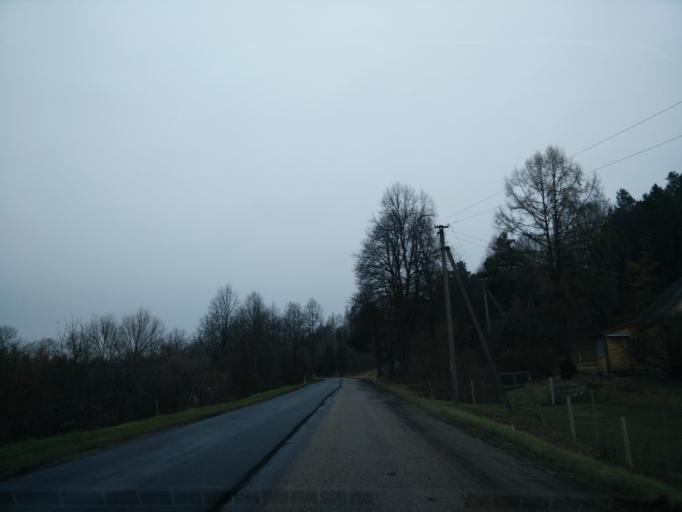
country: LT
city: Ariogala
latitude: 55.2818
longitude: 23.4480
